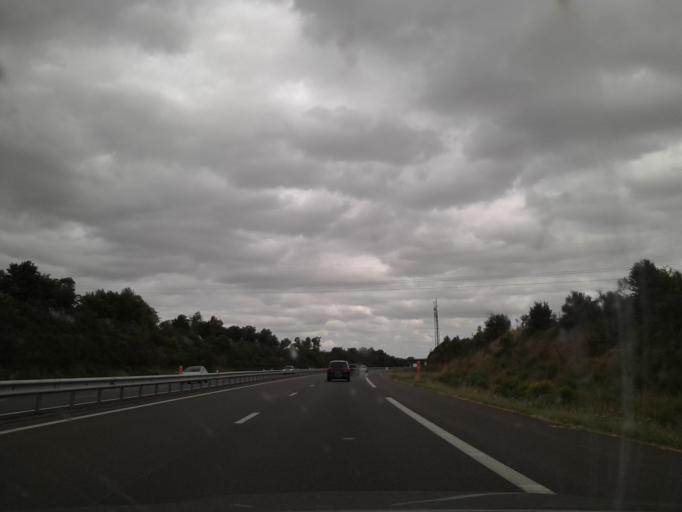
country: FR
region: Centre
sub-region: Departement du Cher
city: Trouy
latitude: 47.0349
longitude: 2.3691
